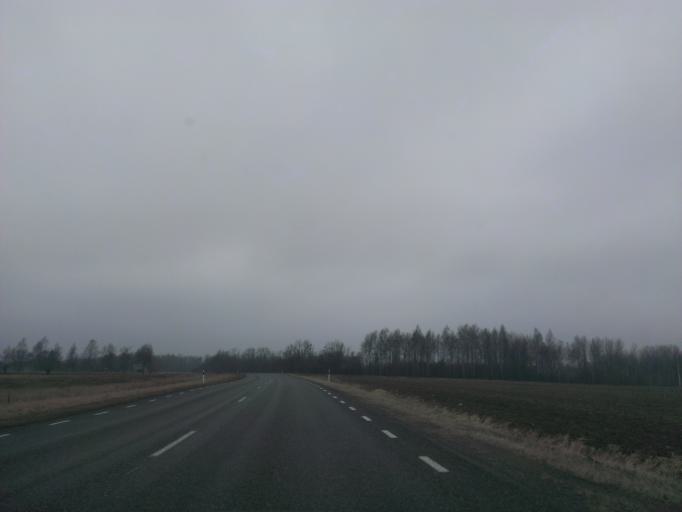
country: EE
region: Paernumaa
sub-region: Audru vald
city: Audru
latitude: 58.5028
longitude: 24.1192
